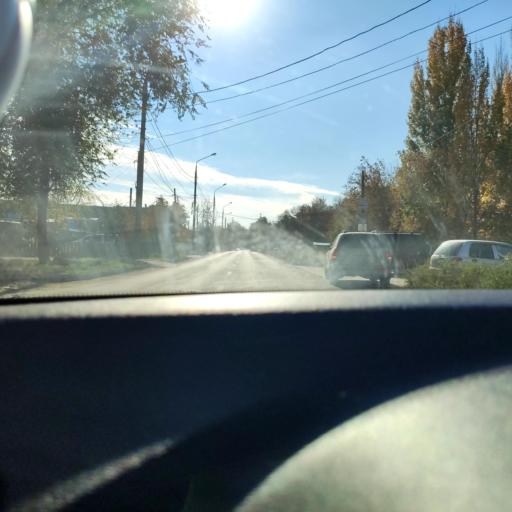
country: RU
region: Samara
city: Smyshlyayevka
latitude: 53.2323
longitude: 50.2990
